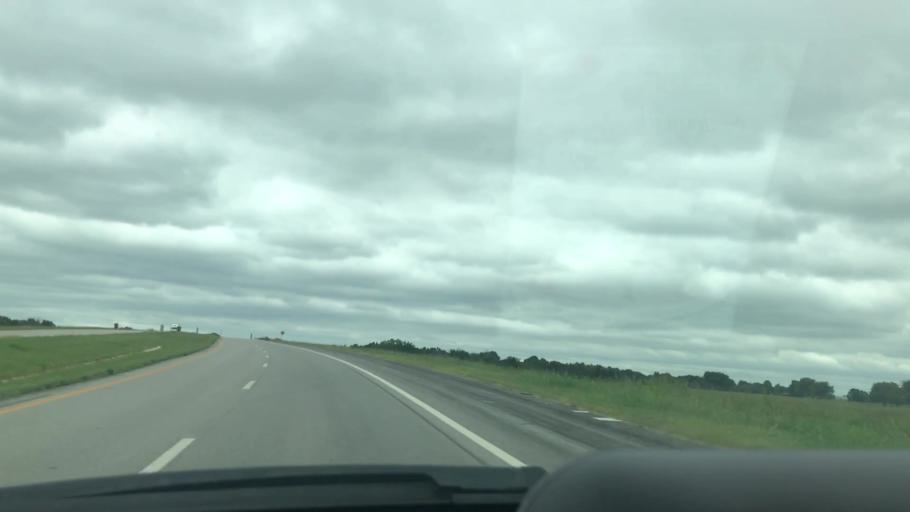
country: US
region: Oklahoma
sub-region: Mayes County
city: Pryor
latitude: 36.3705
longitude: -95.2932
